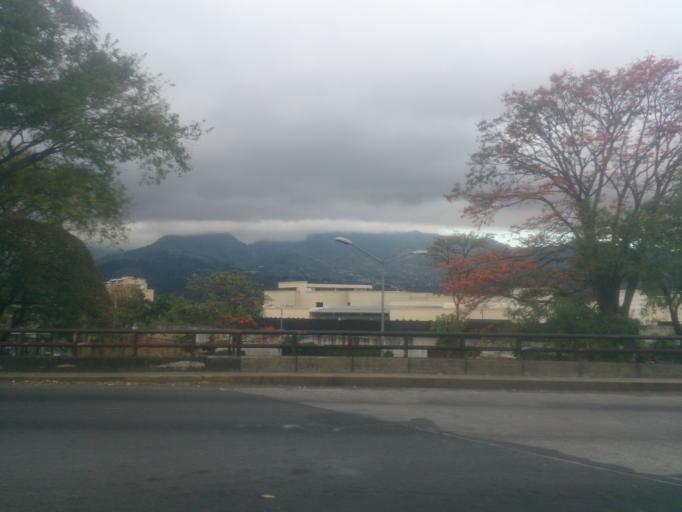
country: CR
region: San Jose
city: San Rafael
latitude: 9.9388
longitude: -84.1166
